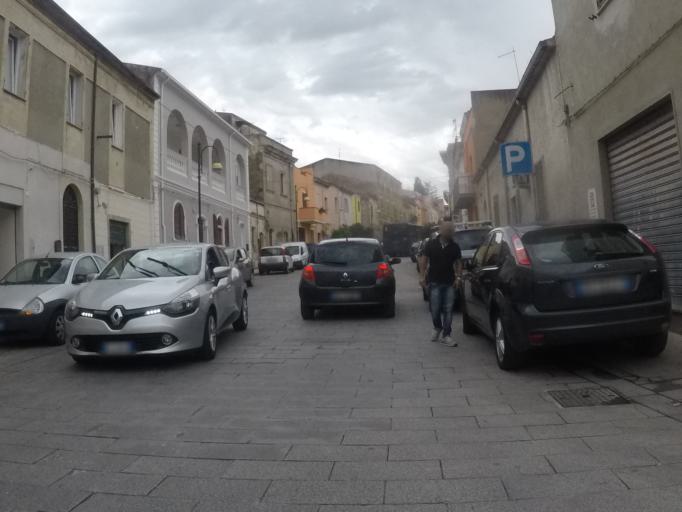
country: IT
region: Sardinia
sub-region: Provincia di Sassari
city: Sorso
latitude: 40.7990
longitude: 8.5810
